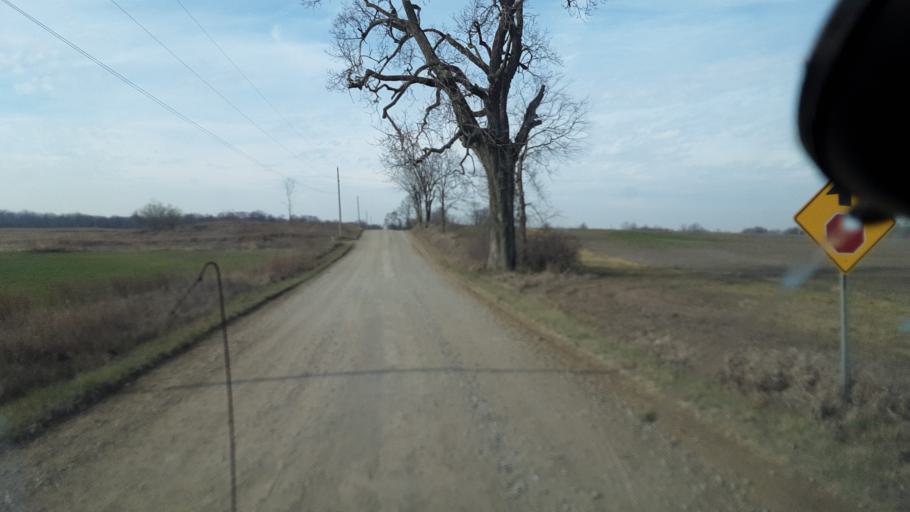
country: US
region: Indiana
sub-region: Allen County
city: Harlan
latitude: 41.2697
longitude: -84.8628
